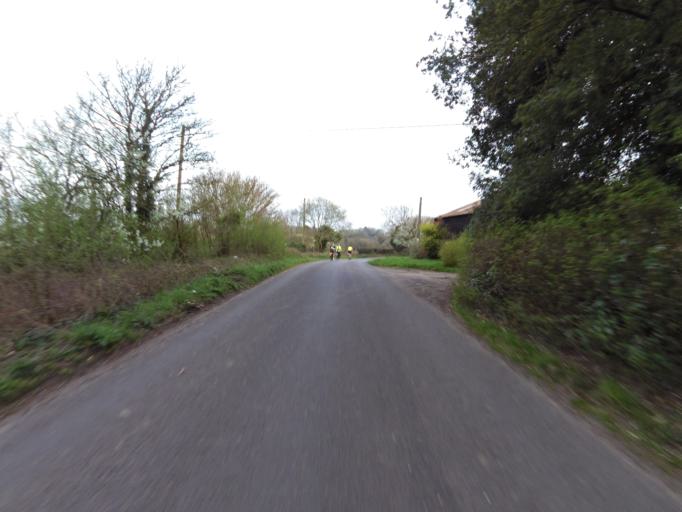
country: GB
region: England
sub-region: Suffolk
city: Kesgrave
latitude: 52.1446
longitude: 1.2373
